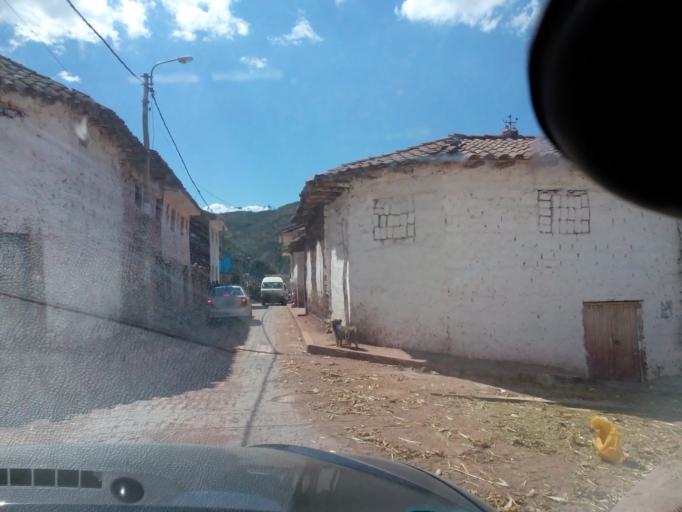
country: PE
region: Cusco
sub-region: Provincia de Anta
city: Huarocondo
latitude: -13.4164
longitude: -72.2084
